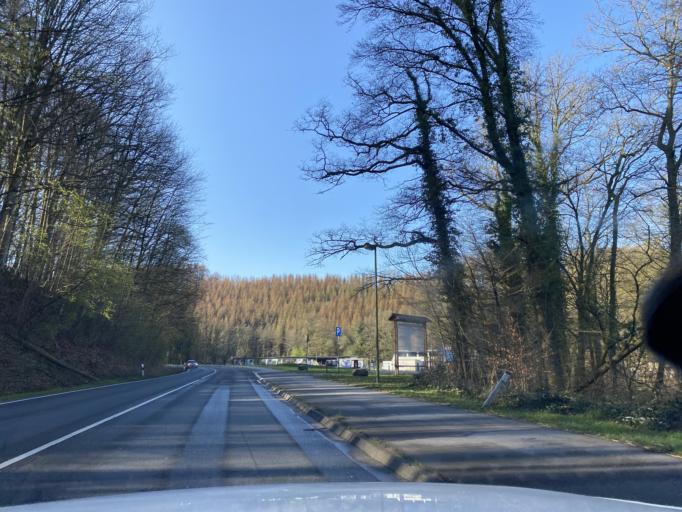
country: DE
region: North Rhine-Westphalia
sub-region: Regierungsbezirk Koln
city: Odenthal
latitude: 51.0295
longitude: 7.1167
